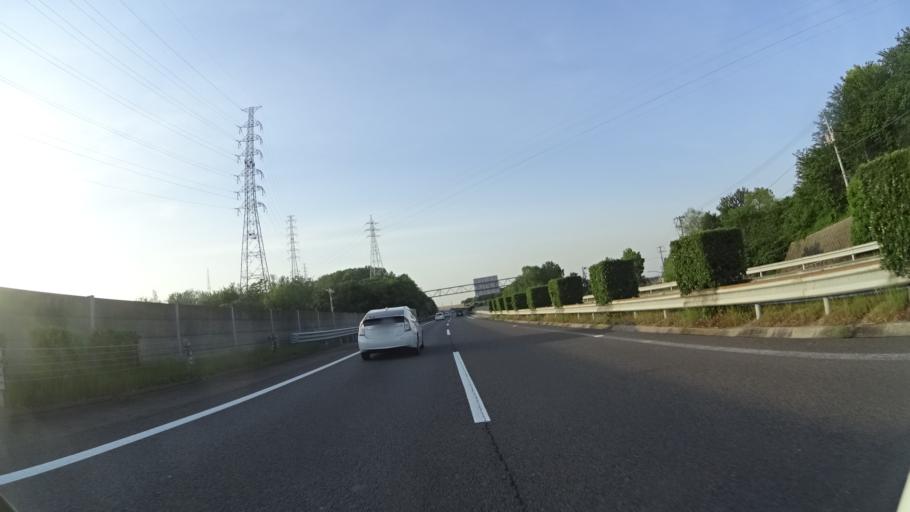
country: JP
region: Kagawa
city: Sakaidecho
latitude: 34.3088
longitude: 133.8393
